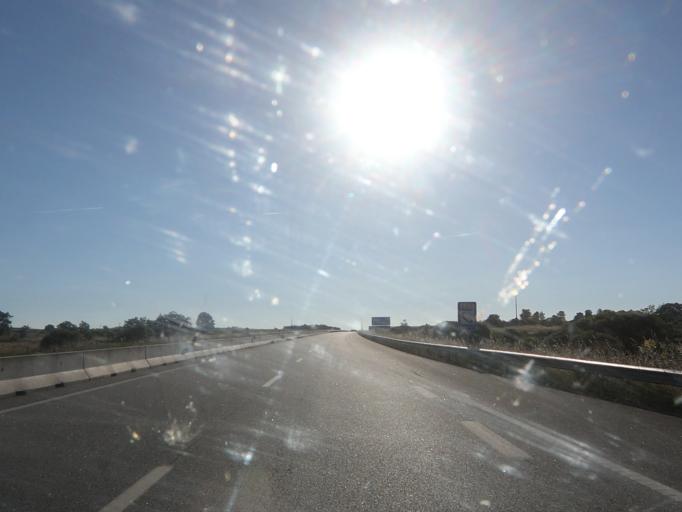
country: ES
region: Castille and Leon
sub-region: Provincia de Salamanca
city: Fuentes de Onoro
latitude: 40.6083
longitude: -6.9886
